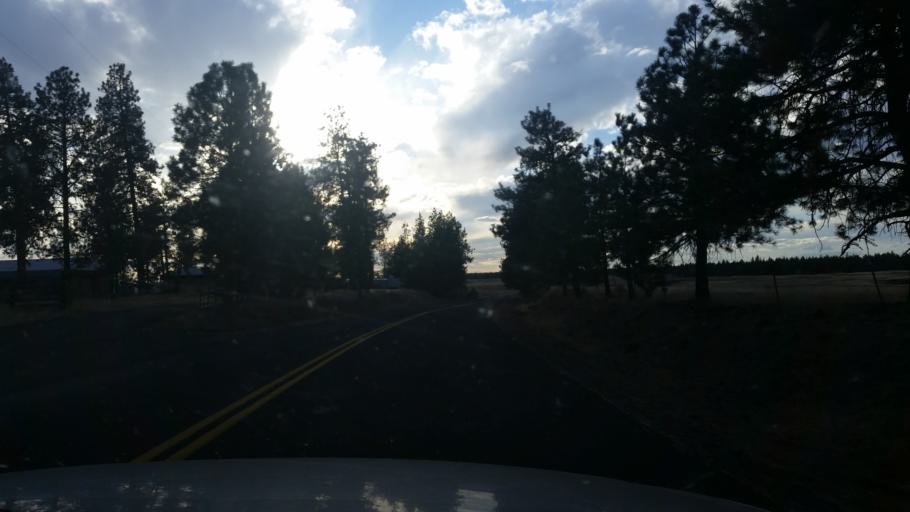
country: US
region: Washington
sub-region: Spokane County
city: Medical Lake
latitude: 47.4497
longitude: -117.7919
